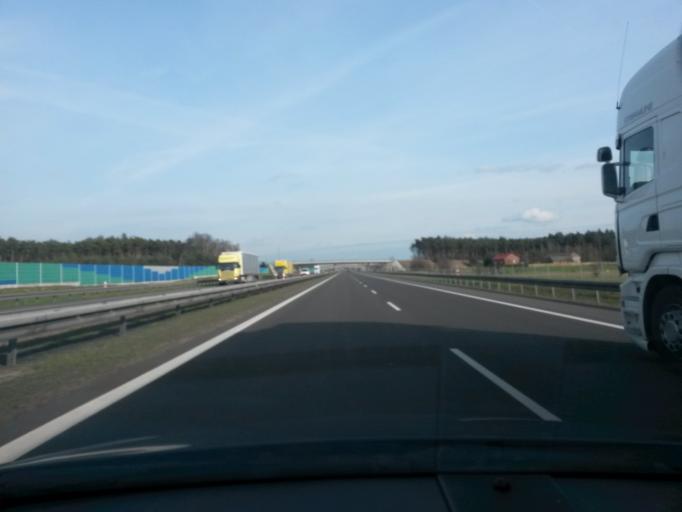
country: PL
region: Greater Poland Voivodeship
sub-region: Powiat koninski
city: Stare Miasto
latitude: 52.1754
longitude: 18.1418
